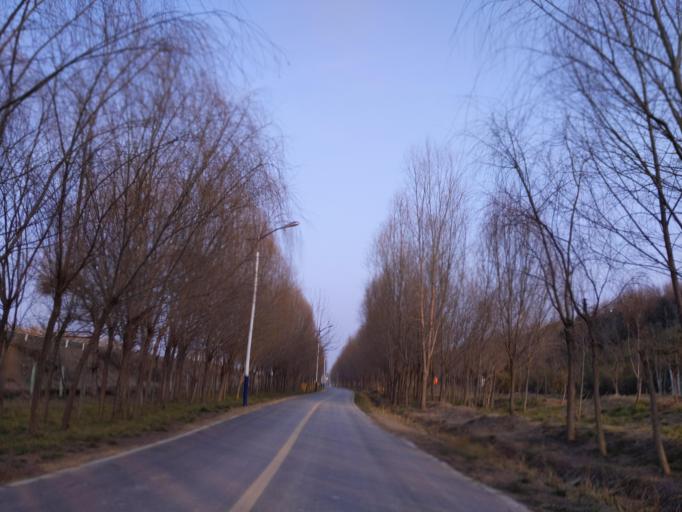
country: CN
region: Henan Sheng
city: Puyang
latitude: 35.8211
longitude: 115.0062
